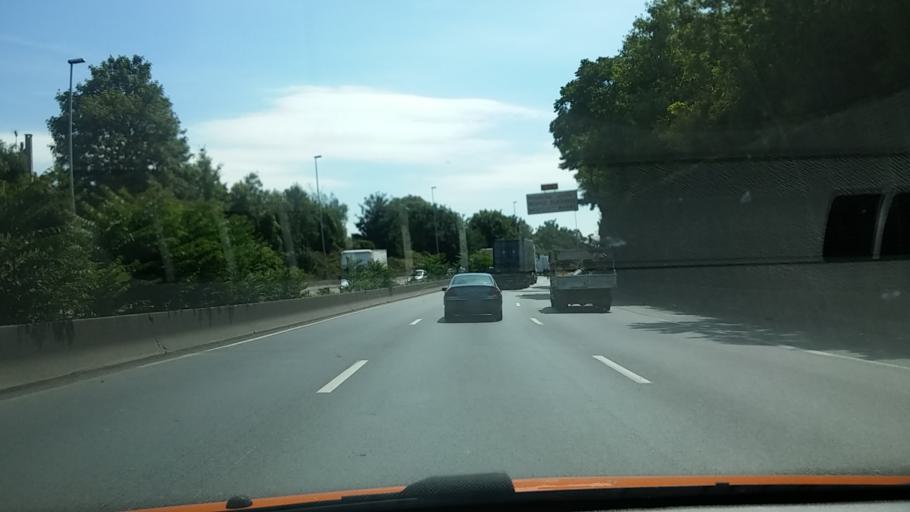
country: FR
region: Ile-de-France
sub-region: Departement du Val-de-Marne
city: Fontenay-sous-Bois
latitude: 48.8710
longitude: 2.4821
